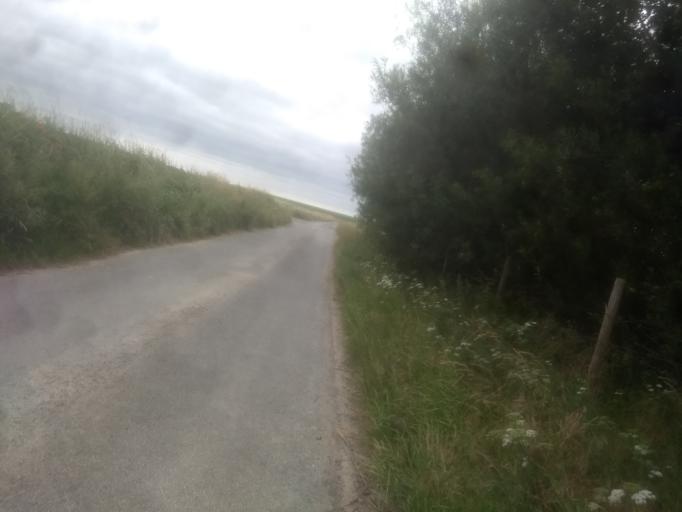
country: FR
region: Nord-Pas-de-Calais
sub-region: Departement du Pas-de-Calais
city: Mont-Saint-Eloi
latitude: 50.3558
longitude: 2.7076
